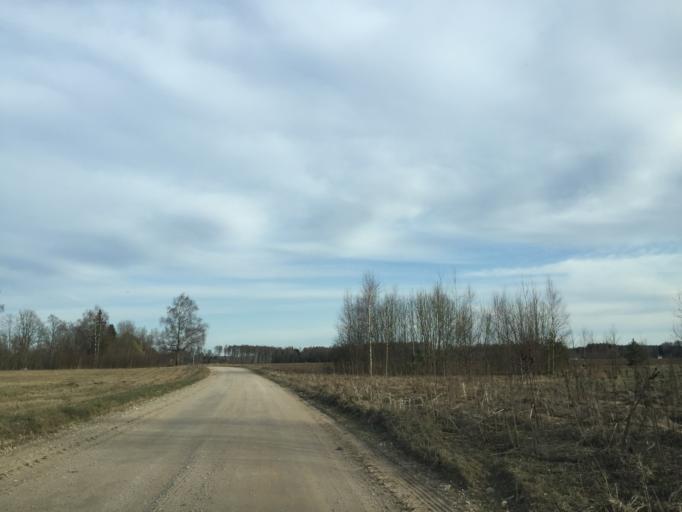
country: LV
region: Kegums
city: Kegums
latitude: 56.7979
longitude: 24.7505
